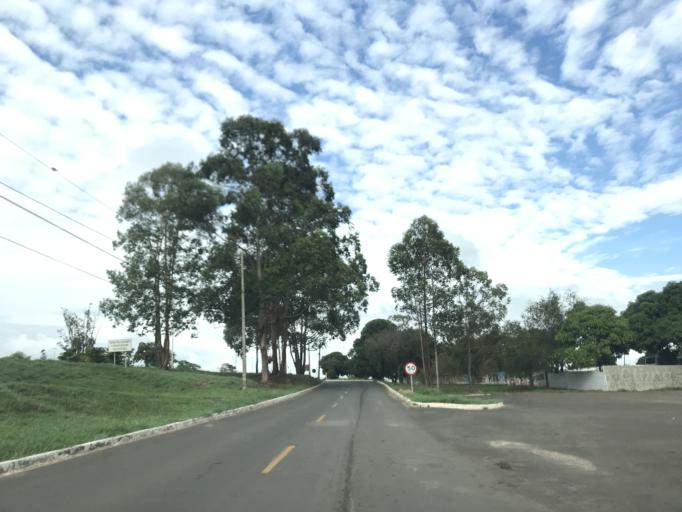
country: BR
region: Federal District
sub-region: Brasilia
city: Brasilia
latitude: -15.6565
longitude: -47.7865
